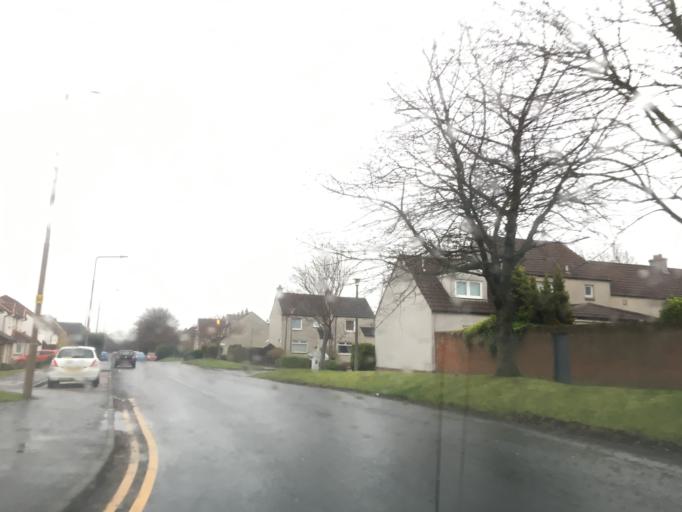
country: GB
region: Scotland
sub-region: Edinburgh
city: Currie
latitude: 55.9351
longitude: -3.3044
